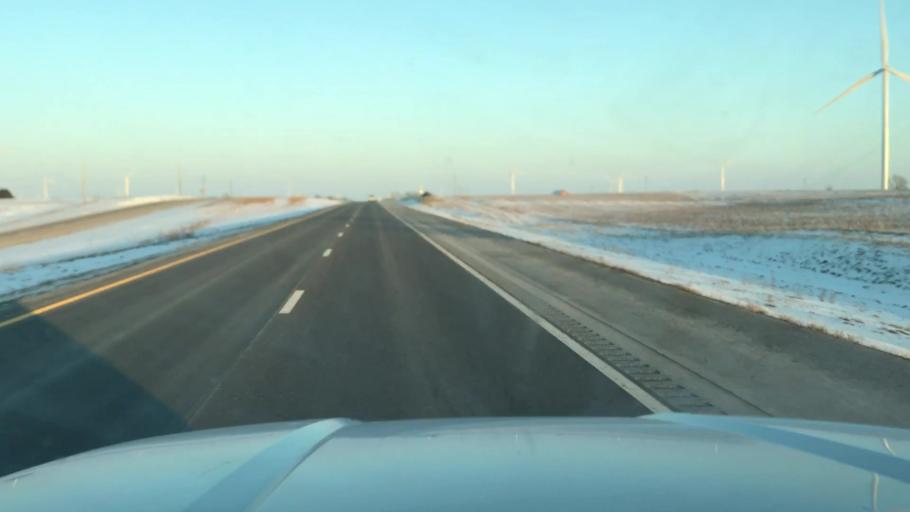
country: US
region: Missouri
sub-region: DeKalb County
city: Maysville
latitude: 39.7617
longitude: -94.4373
